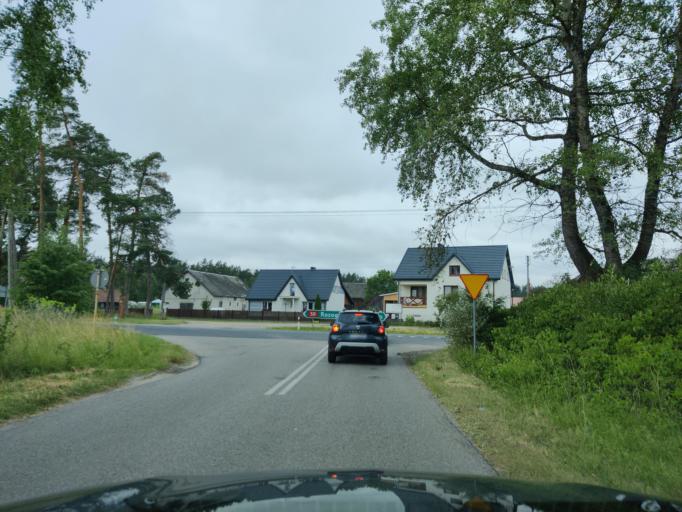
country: PL
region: Warmian-Masurian Voivodeship
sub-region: Powiat szczycienski
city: Rozogi
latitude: 53.5156
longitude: 21.3780
